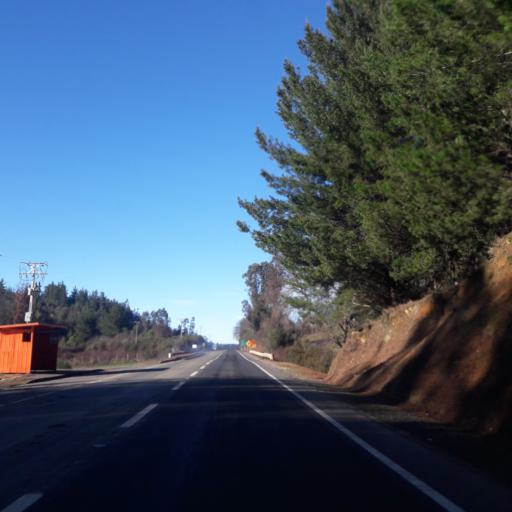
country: CL
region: Biobio
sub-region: Provincia de Biobio
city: La Laja
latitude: -37.3015
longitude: -72.9279
